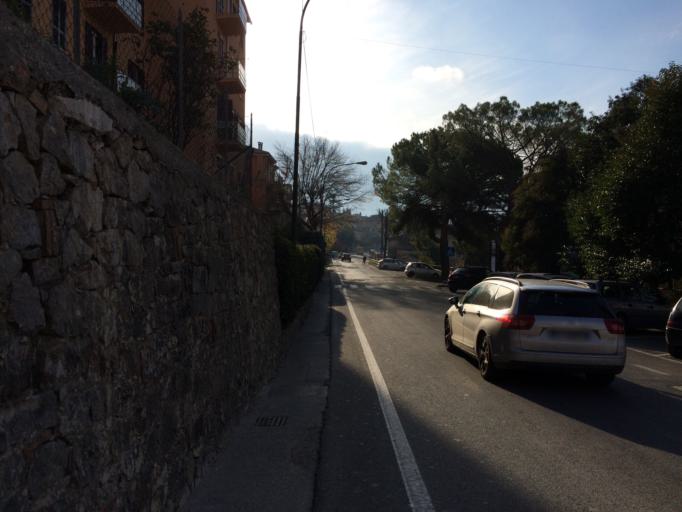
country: IT
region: Umbria
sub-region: Provincia di Terni
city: Amelia
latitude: 42.5518
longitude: 12.4177
